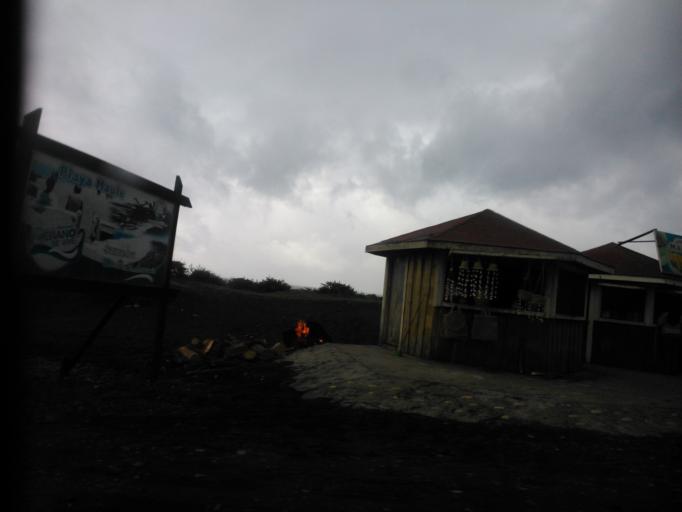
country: CL
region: Araucania
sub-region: Provincia de Cautin
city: Carahue
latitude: -38.8132
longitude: -73.4004
